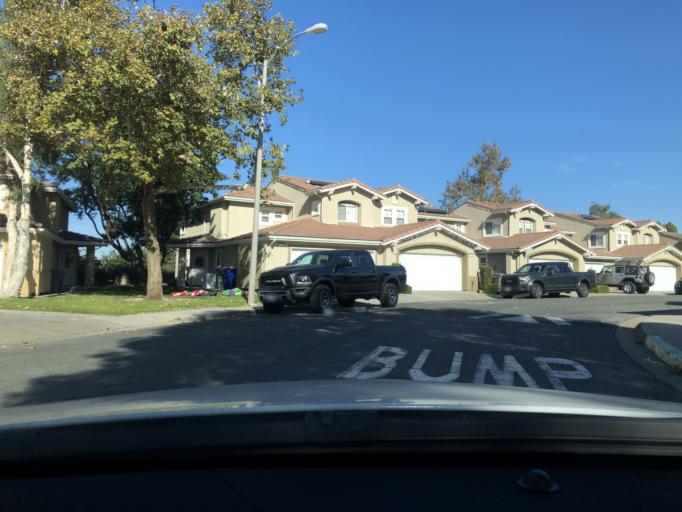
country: US
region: California
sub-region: San Diego County
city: Lemon Grove
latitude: 32.7405
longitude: -117.0610
